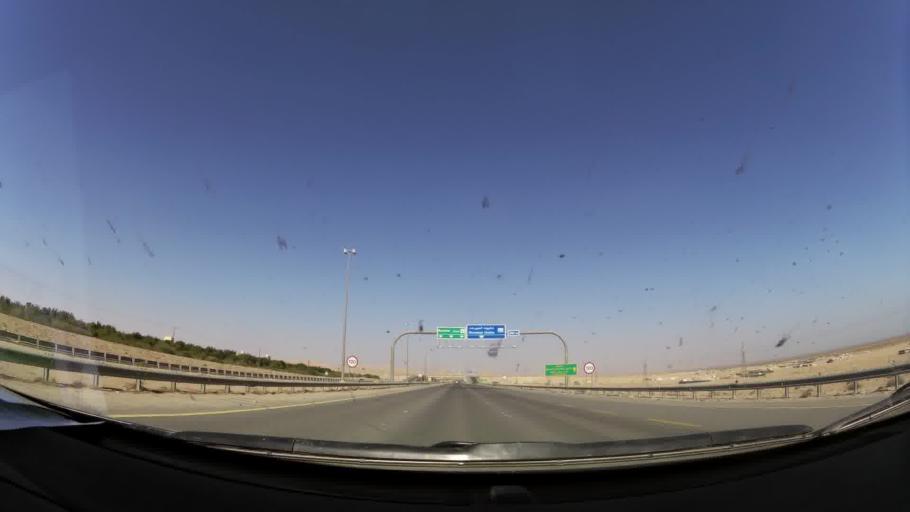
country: KW
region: Muhafazat al Jahra'
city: Al Jahra'
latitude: 29.4675
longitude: 47.7653
